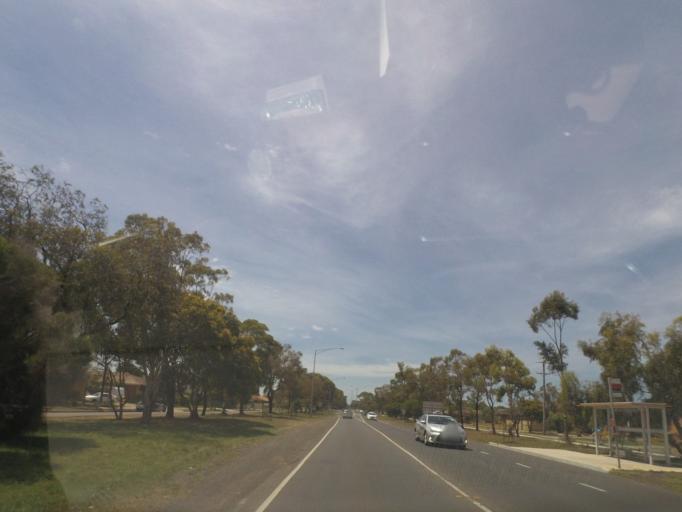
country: AU
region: Victoria
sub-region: Wyndham
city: Werribee
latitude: -37.8949
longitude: 144.6354
